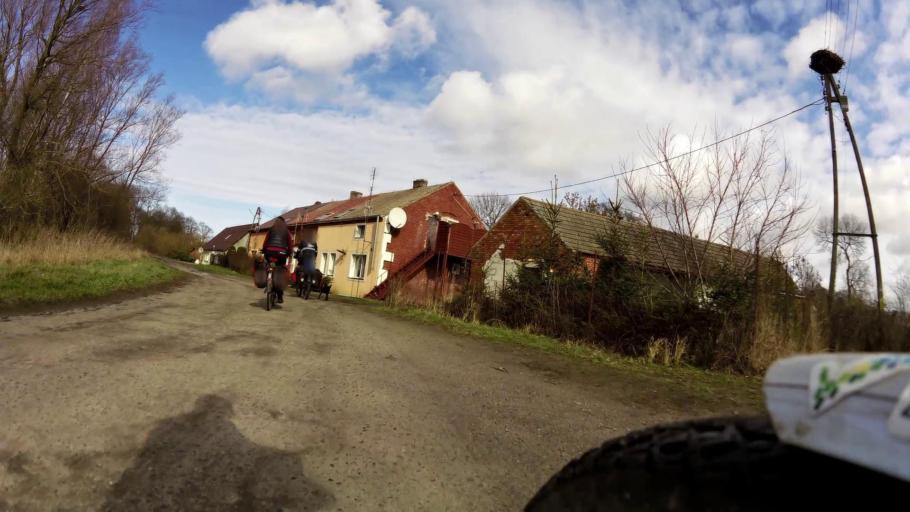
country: PL
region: West Pomeranian Voivodeship
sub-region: Powiat kamienski
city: Kamien Pomorski
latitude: 53.9952
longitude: 14.7711
